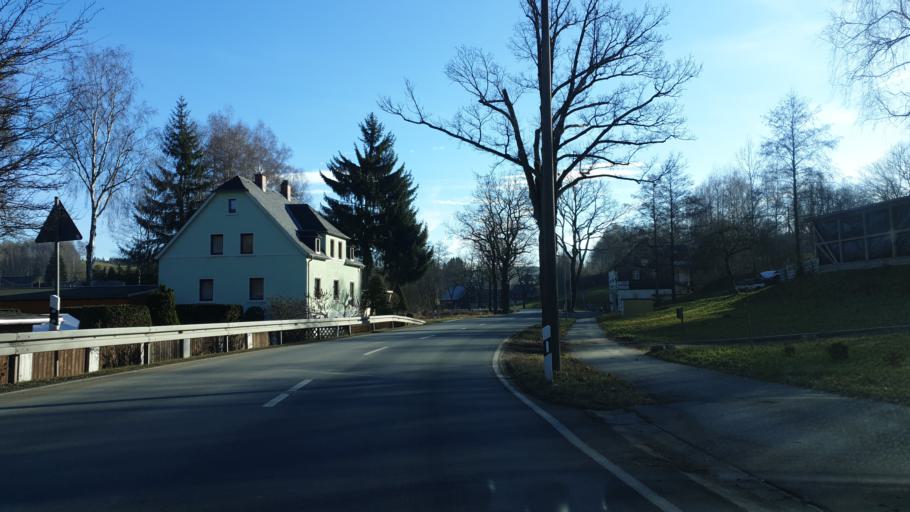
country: DE
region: Saxony
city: Adorf
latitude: 50.2955
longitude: 12.2617
